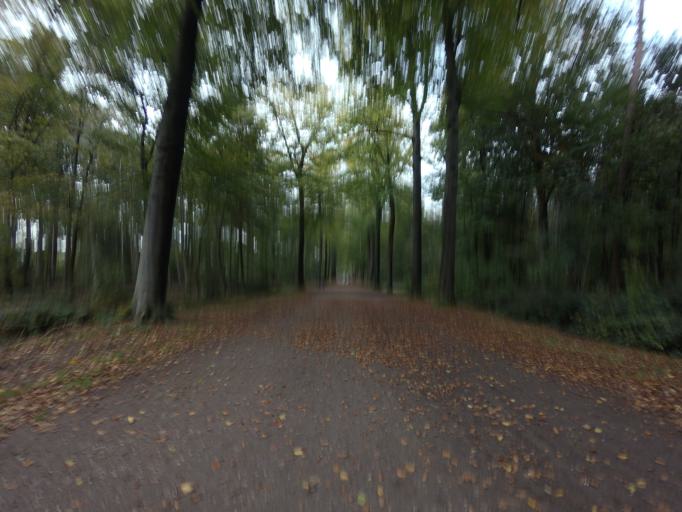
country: NL
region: North Brabant
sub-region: Gemeente Breda
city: Breda
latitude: 51.5609
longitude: 4.7598
